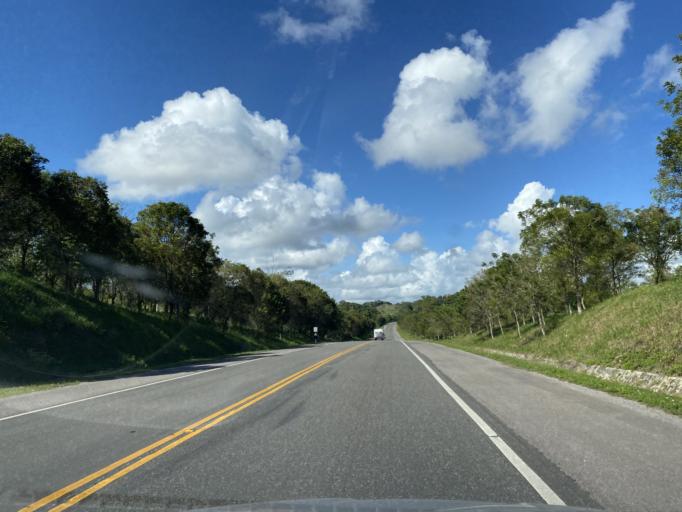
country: DO
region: Monte Plata
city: Majagual
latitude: 19.0276
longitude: -69.8239
